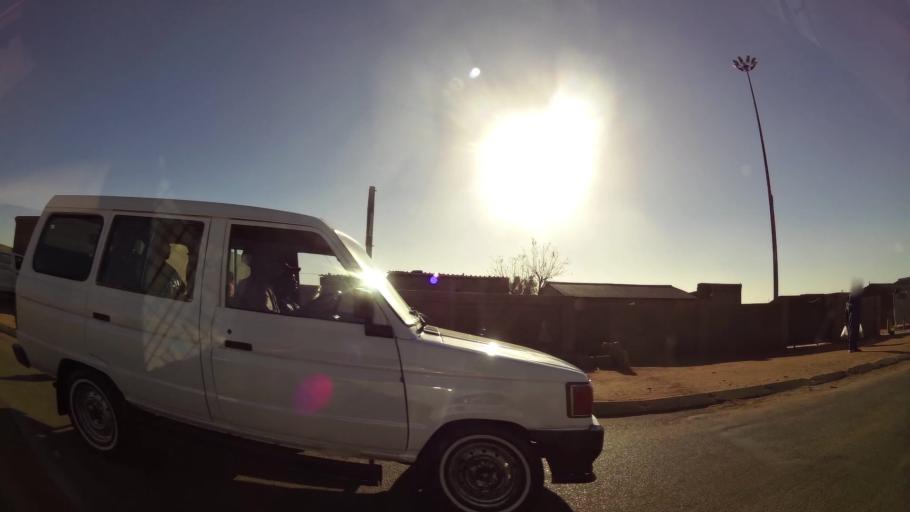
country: ZA
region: Gauteng
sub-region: Ekurhuleni Metropolitan Municipality
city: Tembisa
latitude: -26.0162
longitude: 28.2249
